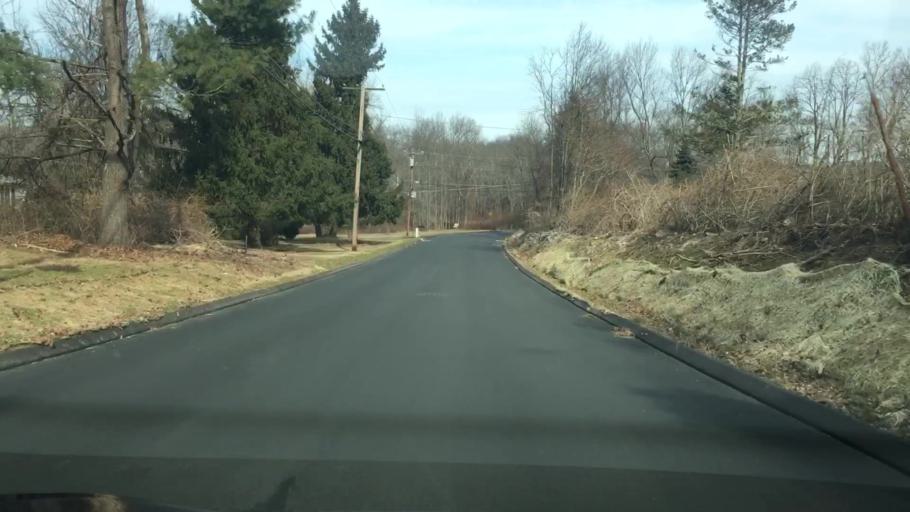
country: US
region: New York
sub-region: Putnam County
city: Peach Lake
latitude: 41.3794
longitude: -73.5197
